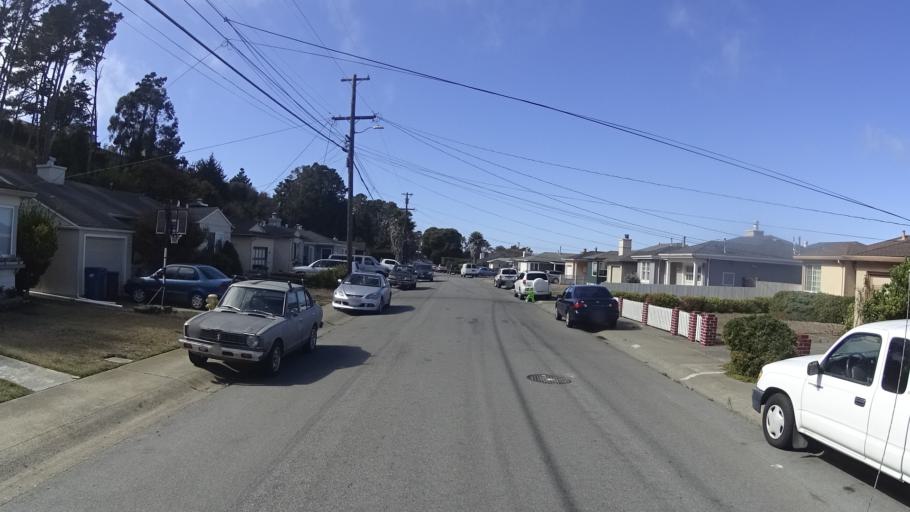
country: US
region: California
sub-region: San Mateo County
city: Broadmoor
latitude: 37.6915
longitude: -122.4827
